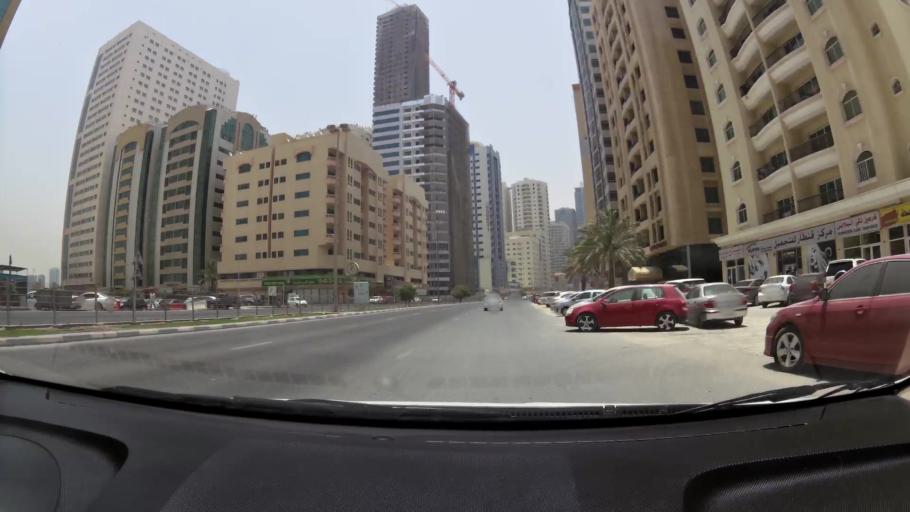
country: AE
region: Ash Shariqah
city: Sharjah
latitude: 25.3288
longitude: 55.3746
